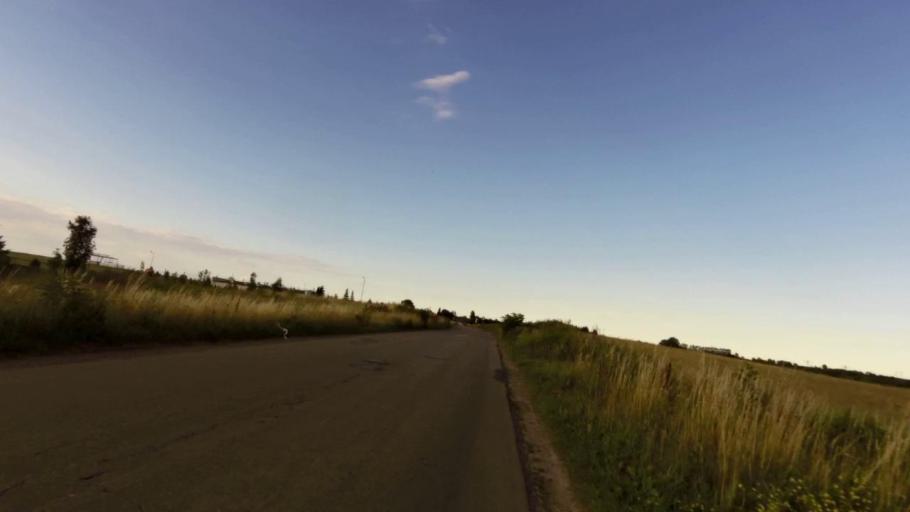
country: PL
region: West Pomeranian Voivodeship
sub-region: Powiat slawienski
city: Darlowo
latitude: 54.4058
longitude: 16.3867
